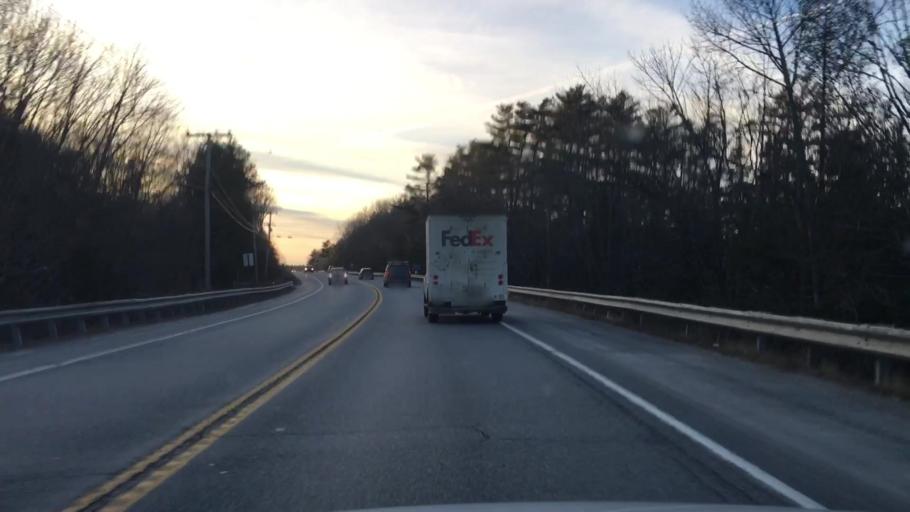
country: US
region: Maine
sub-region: Penobscot County
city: Holden
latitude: 44.7557
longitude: -68.6660
